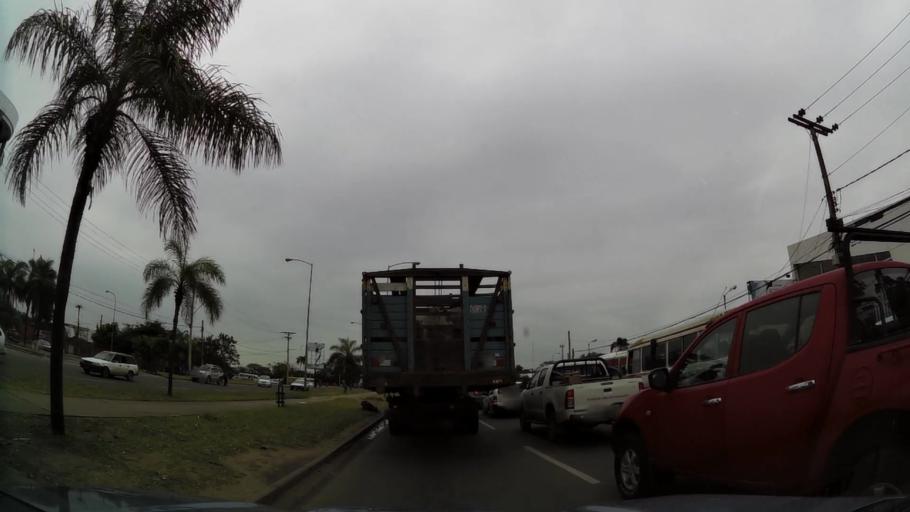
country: BO
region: Santa Cruz
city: Santa Cruz de la Sierra
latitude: -17.8128
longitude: -63.2092
